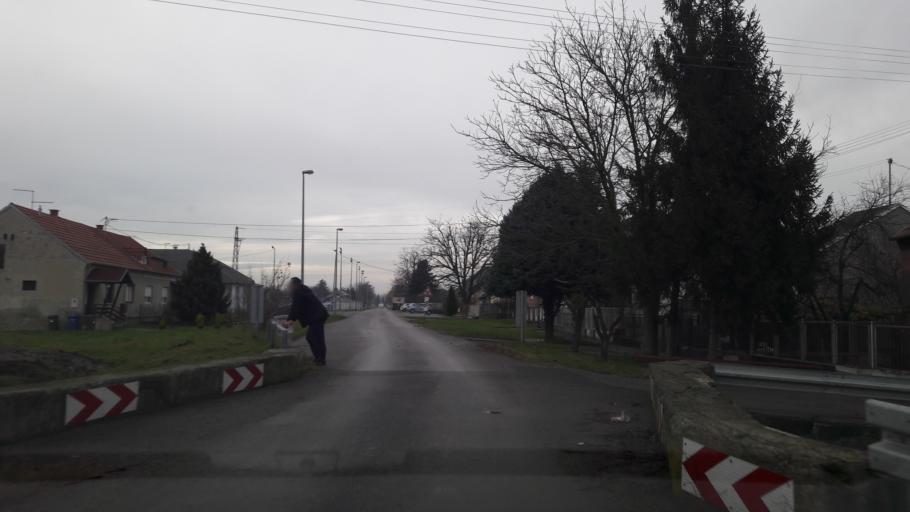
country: HR
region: Osjecko-Baranjska
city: Visnjevac
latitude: 45.5593
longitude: 18.6180
